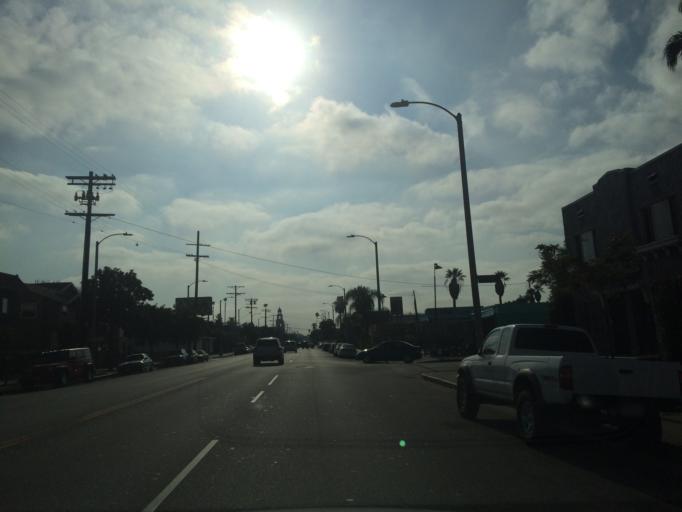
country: US
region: California
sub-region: Los Angeles County
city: Los Angeles
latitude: 34.0327
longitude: -118.2985
